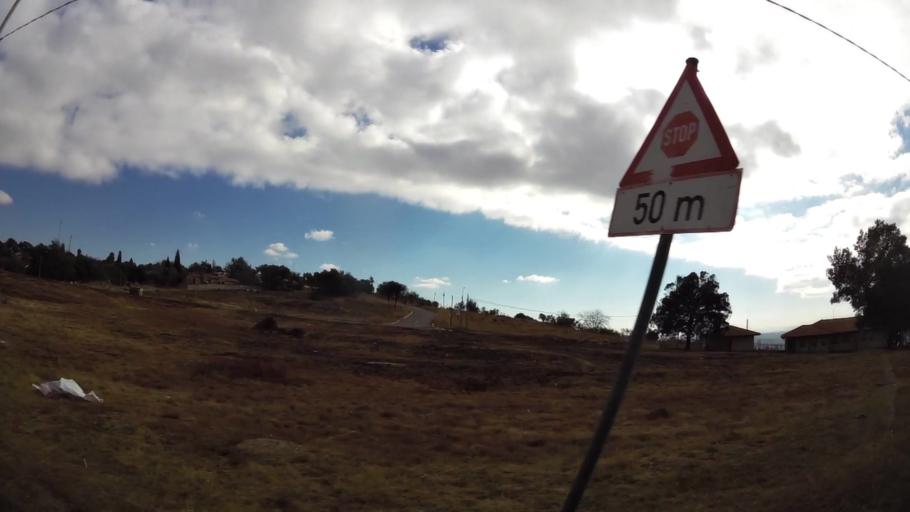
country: ZA
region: Gauteng
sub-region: City of Johannesburg Metropolitan Municipality
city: Roodepoort
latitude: -26.1073
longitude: 27.8662
